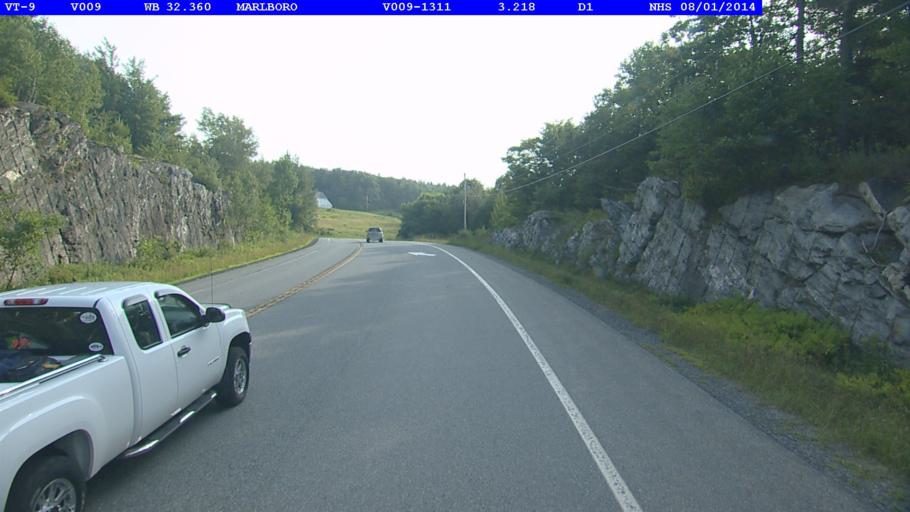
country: US
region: Vermont
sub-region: Windham County
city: Dover
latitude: 42.8625
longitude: -72.7608
